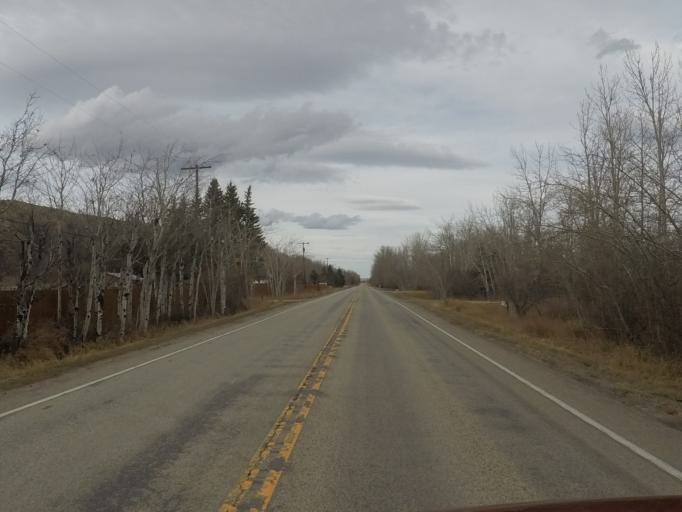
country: US
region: Montana
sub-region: Carbon County
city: Red Lodge
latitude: 45.2169
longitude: -109.2418
